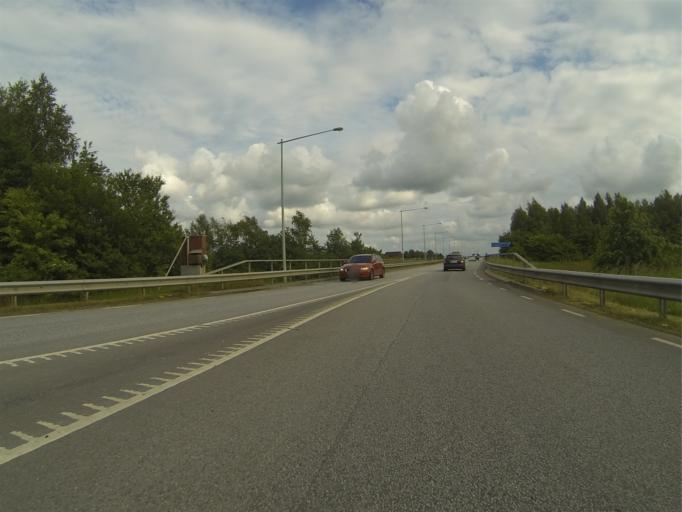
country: SE
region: Skane
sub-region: Staffanstorps Kommun
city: Staffanstorp
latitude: 55.6413
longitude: 13.2332
